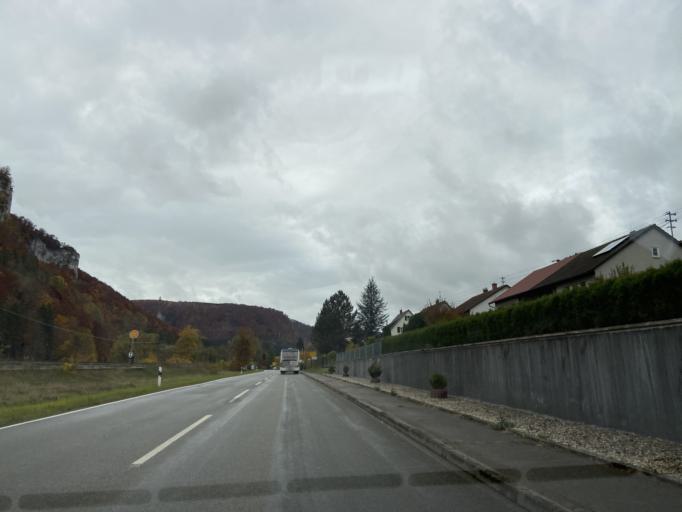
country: DE
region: Baden-Wuerttemberg
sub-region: Tuebingen Region
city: Schwenningen
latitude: 48.0873
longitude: 9.0427
